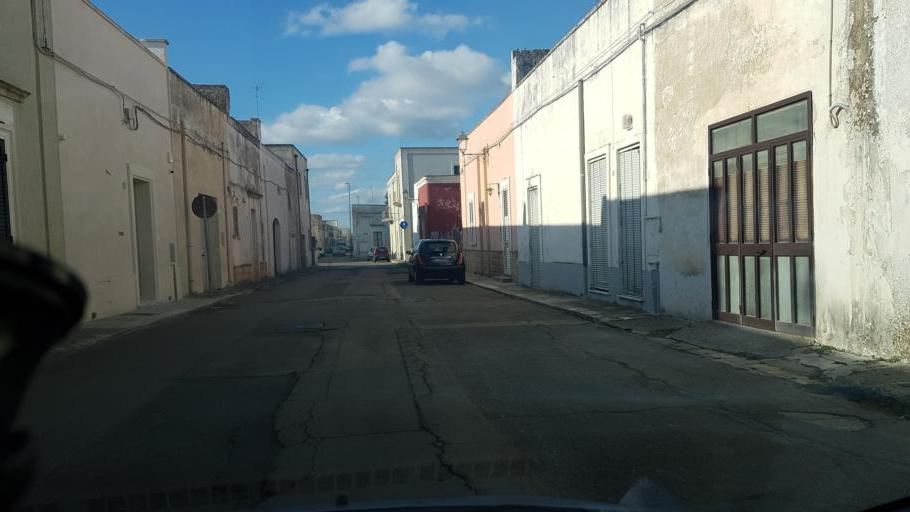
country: IT
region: Apulia
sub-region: Provincia di Lecce
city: Campi Salentina
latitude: 40.4010
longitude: 18.0173
